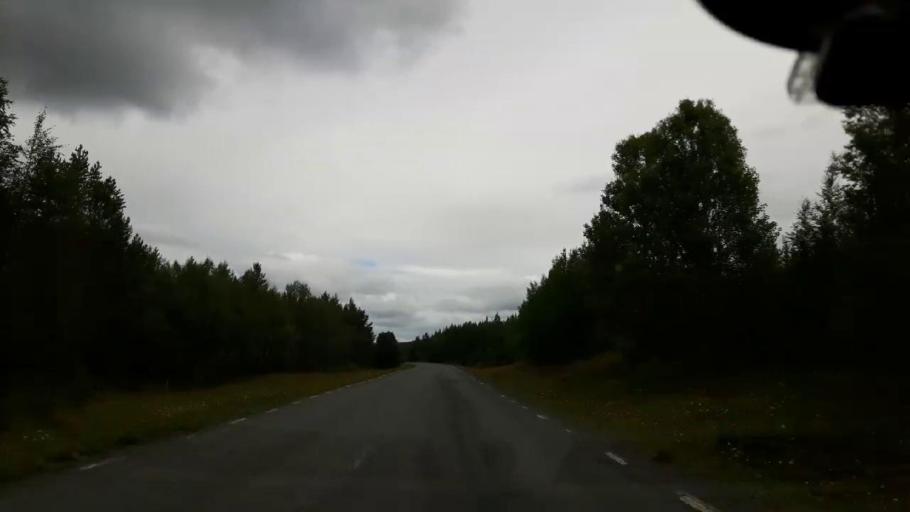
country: SE
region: Jaemtland
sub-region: Krokoms Kommun
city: Valla
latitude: 63.6341
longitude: 13.8171
